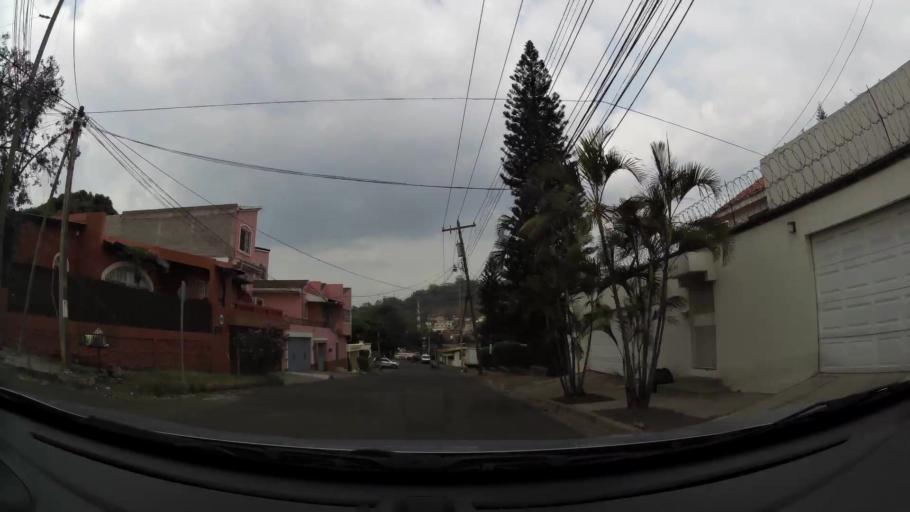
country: HN
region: Francisco Morazan
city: Tegucigalpa
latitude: 14.0942
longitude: -87.1941
